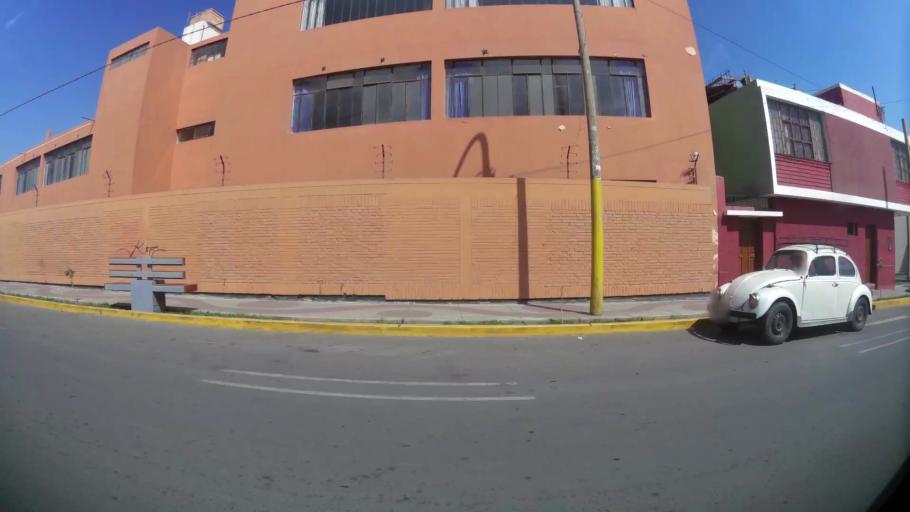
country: PE
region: Lima
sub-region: Huaura
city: Huacho
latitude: -11.1080
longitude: -77.6135
